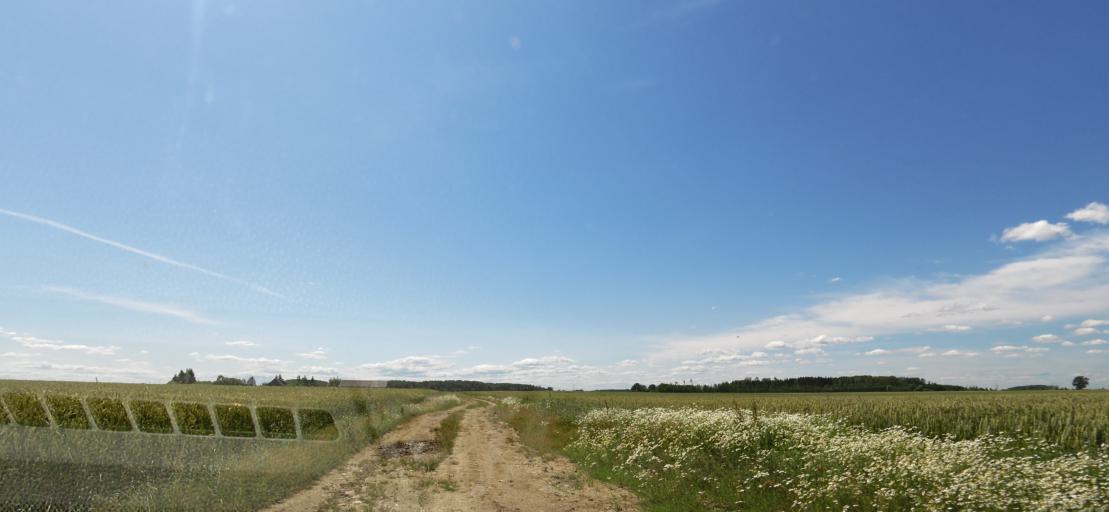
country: LT
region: Panevezys
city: Pasvalys
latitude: 56.2693
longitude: 24.5135
